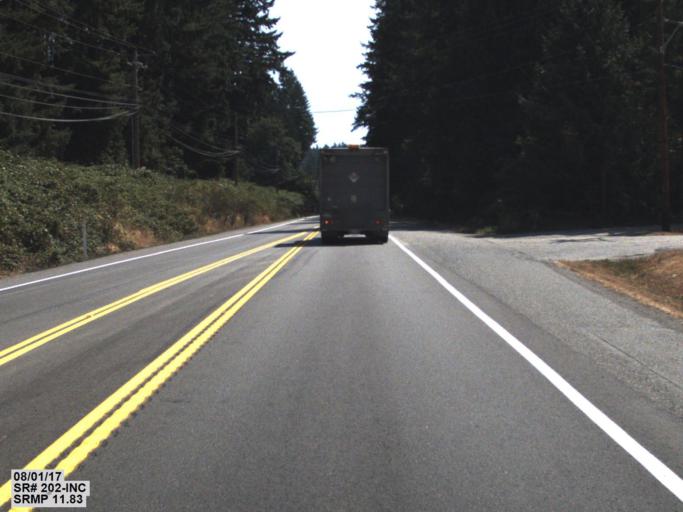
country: US
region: Washington
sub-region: King County
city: Union Hill-Novelty Hill
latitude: 47.6455
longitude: -122.0337
